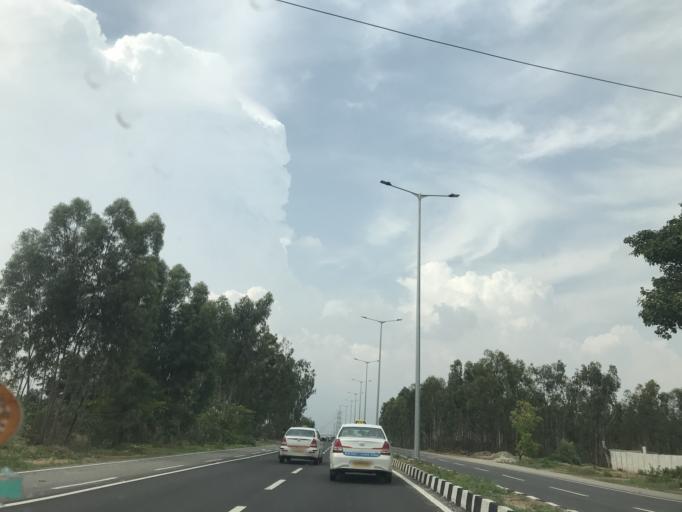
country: IN
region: Karnataka
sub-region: Bangalore Rural
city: Devanhalli
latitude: 13.1610
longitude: 77.6846
